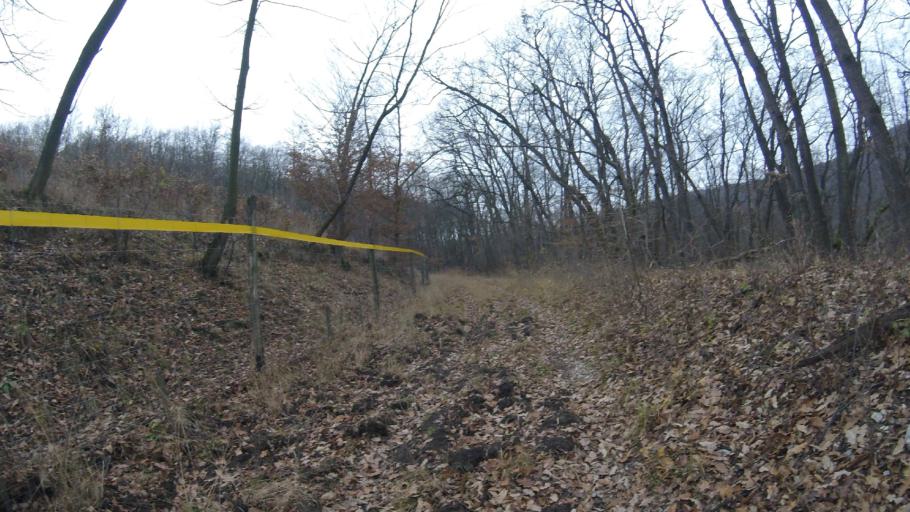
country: HU
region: Komarom-Esztergom
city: Tardos
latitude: 47.6962
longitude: 18.4448
